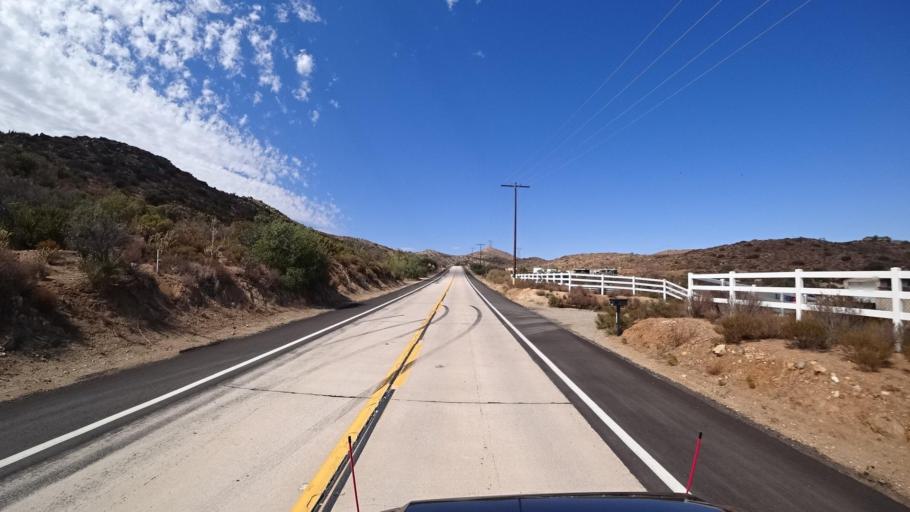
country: MX
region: Baja California
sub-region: Tecate
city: Cereso del Hongo
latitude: 32.6356
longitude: -116.2265
